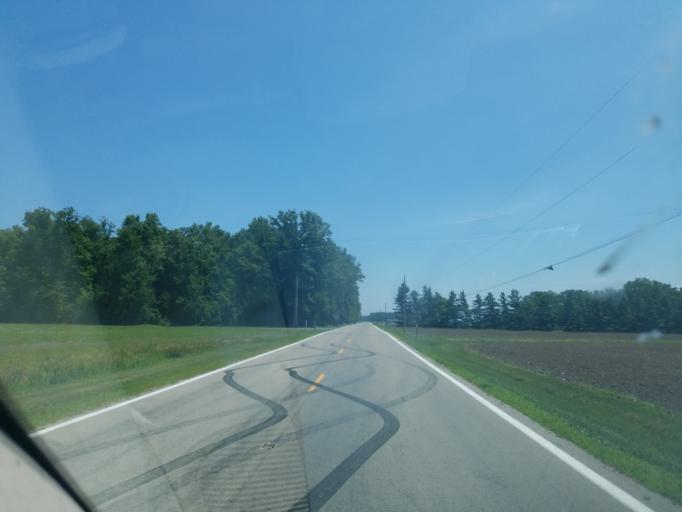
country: US
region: Ohio
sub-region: Allen County
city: Spencerville
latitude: 40.7430
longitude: -84.4114
